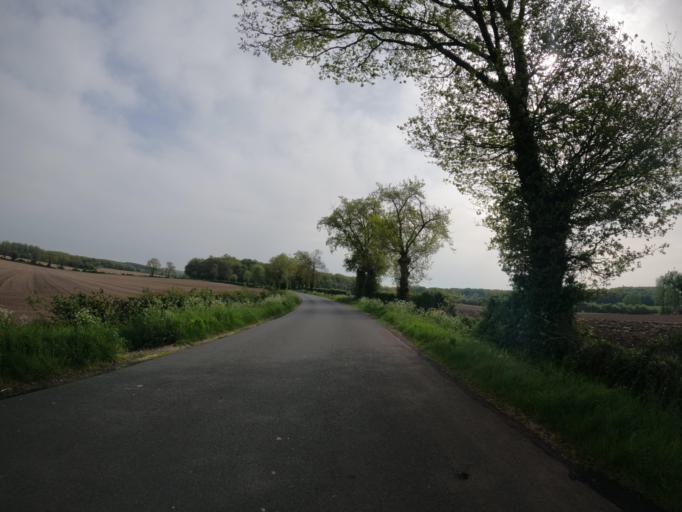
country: FR
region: Poitou-Charentes
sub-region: Departement des Deux-Sevres
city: Moncoutant
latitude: 46.6959
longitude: -0.5393
